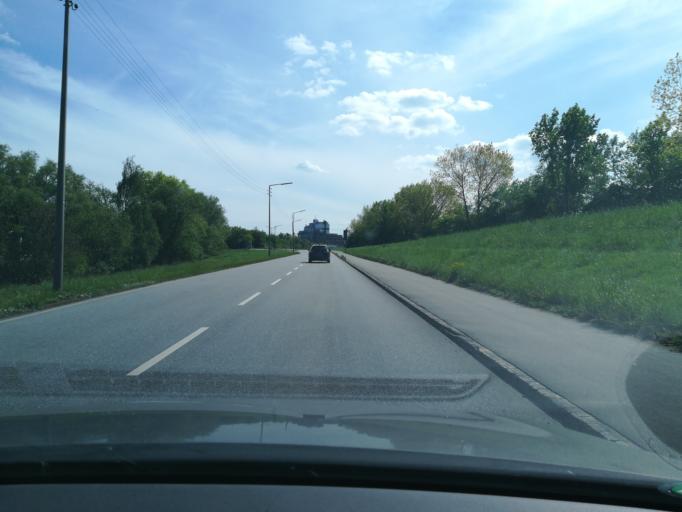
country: DE
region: Hamburg
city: Kleiner Grasbrook
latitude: 53.5094
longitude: 9.9761
